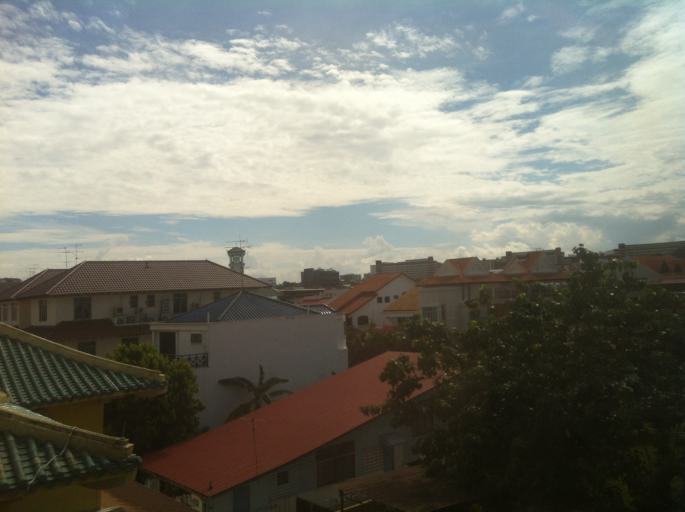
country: SG
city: Singapore
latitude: 1.3214
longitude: 103.9145
